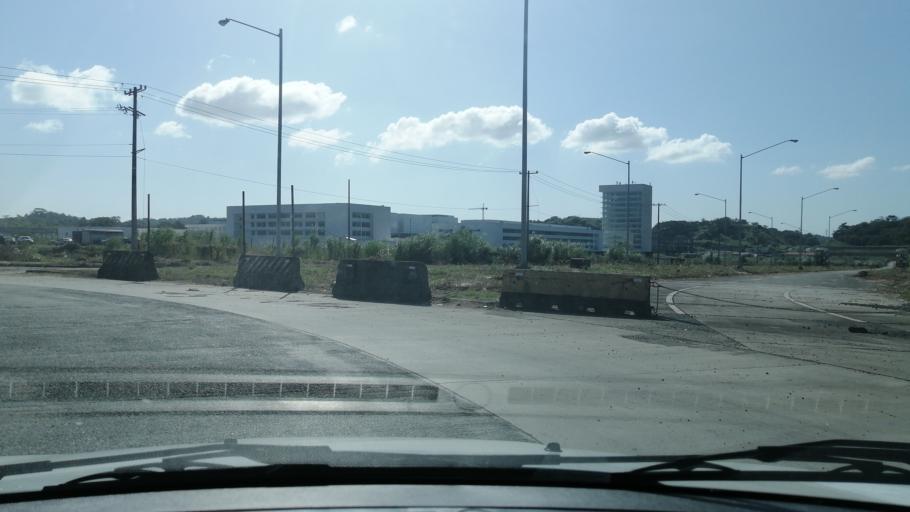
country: PA
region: Panama
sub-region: Distrito de Panama
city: Paraiso
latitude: 9.0277
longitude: -79.5816
